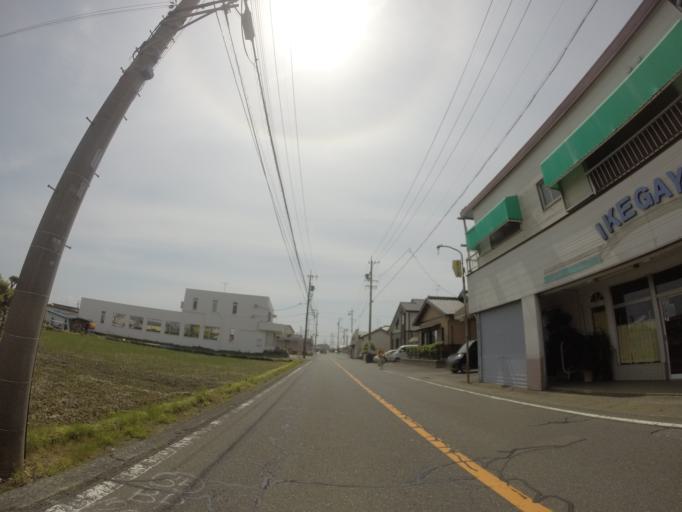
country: JP
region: Shizuoka
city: Fujieda
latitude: 34.8089
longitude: 138.2864
